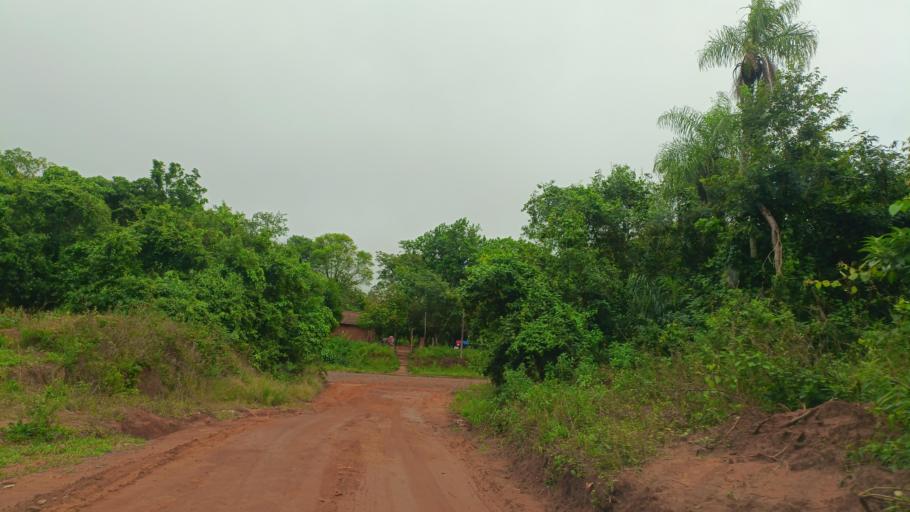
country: PY
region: Misiones
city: Santa Maria
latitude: -26.8793
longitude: -57.0124
